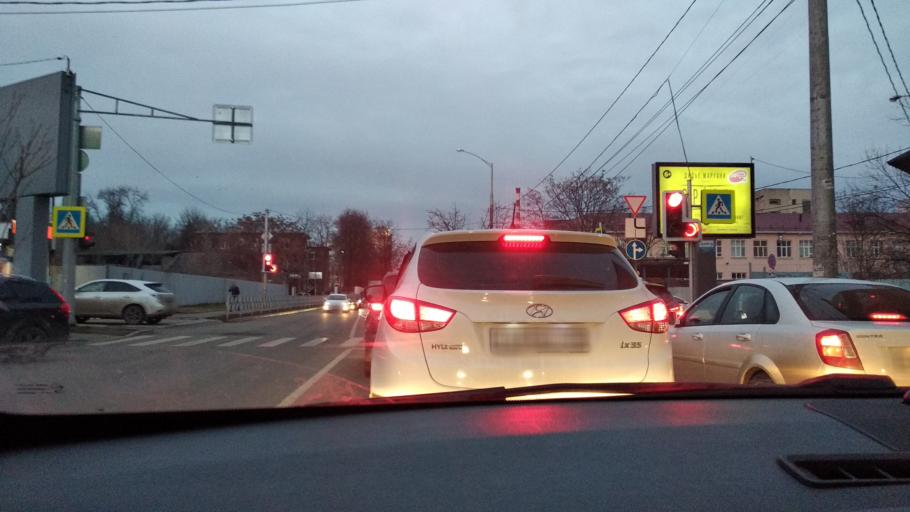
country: RU
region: Krasnodarskiy
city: Krasnodar
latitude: 45.0422
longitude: 38.9741
